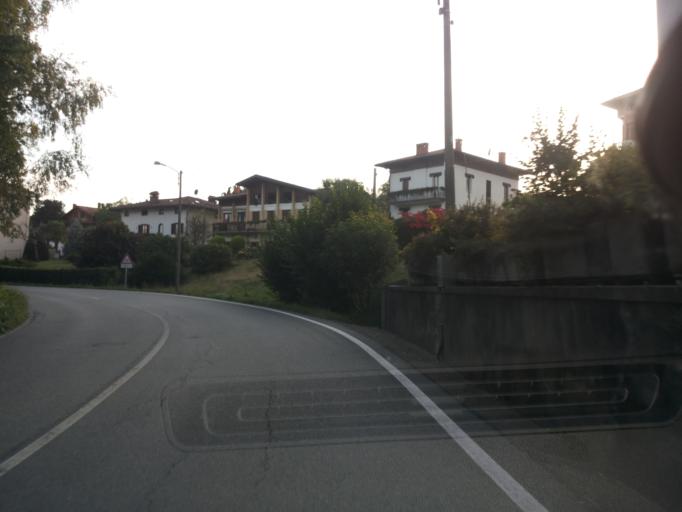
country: IT
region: Piedmont
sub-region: Provincia di Biella
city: Mosso
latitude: 45.6482
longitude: 8.1522
